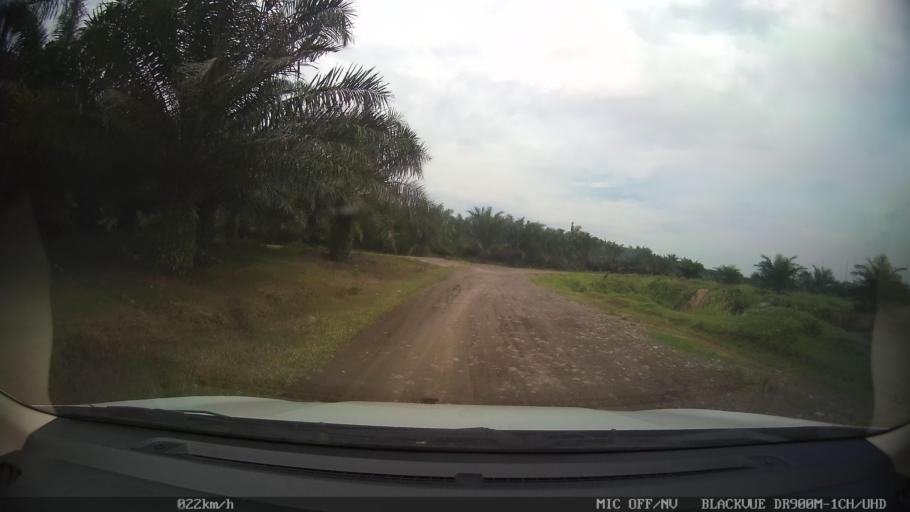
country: ID
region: North Sumatra
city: Sunggal
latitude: 3.6340
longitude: 98.5836
